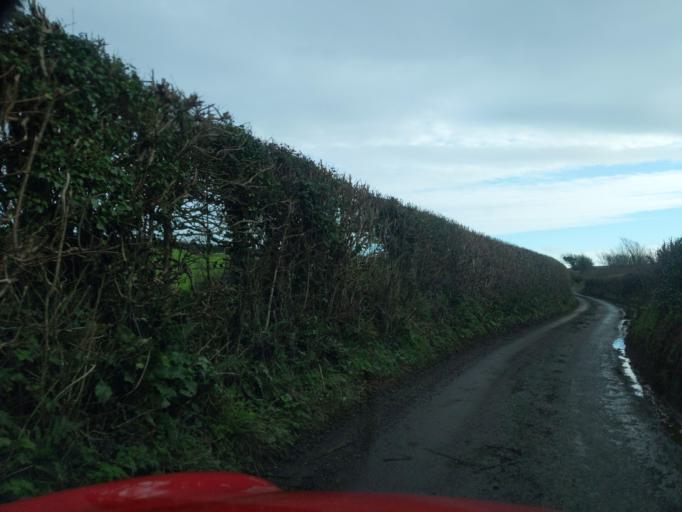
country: GB
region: England
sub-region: Devon
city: Salcombe
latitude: 50.2630
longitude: -3.6858
